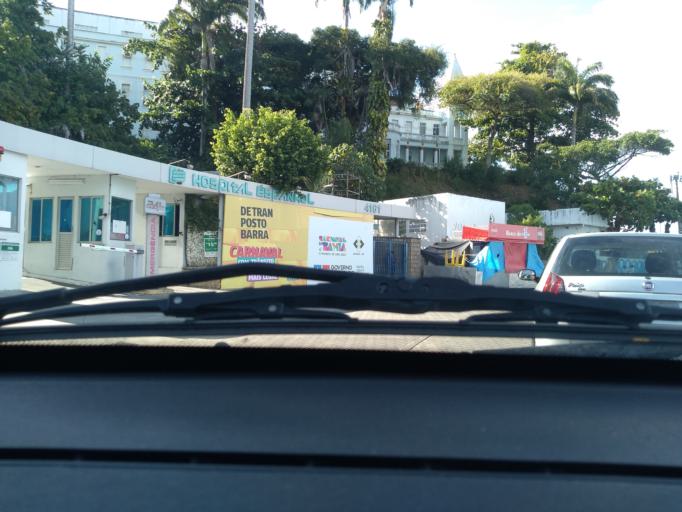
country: BR
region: Bahia
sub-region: Salvador
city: Salvador
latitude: -13.0060
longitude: -38.5329
